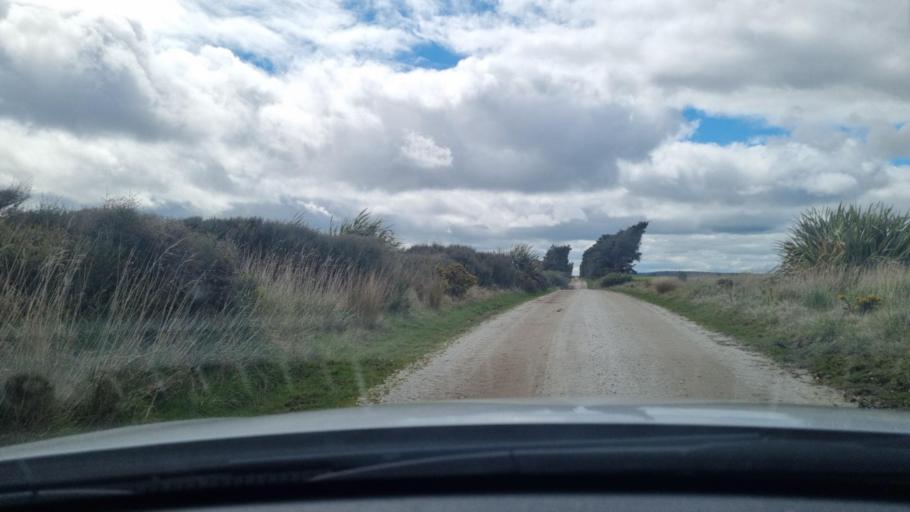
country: NZ
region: Southland
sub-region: Invercargill City
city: Bluff
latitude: -46.5726
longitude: 168.4976
